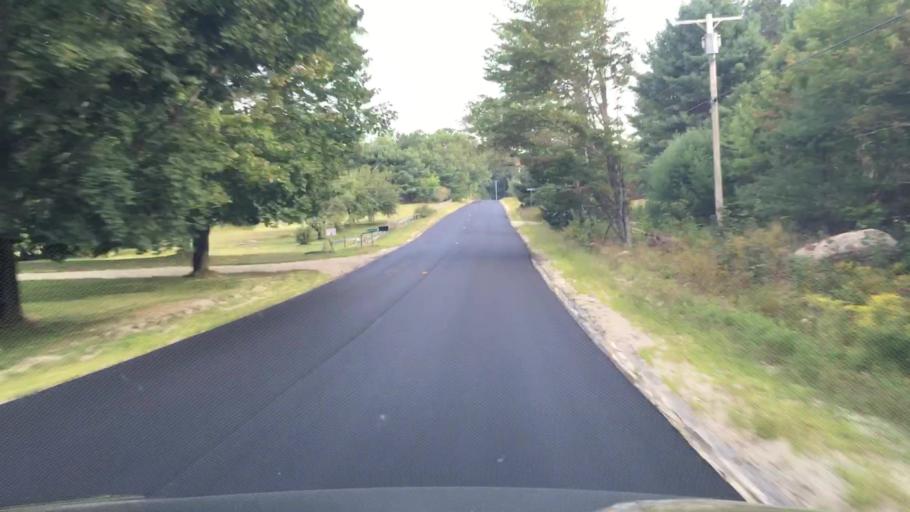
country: US
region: Maine
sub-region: Hancock County
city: Surry
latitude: 44.5282
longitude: -68.6113
